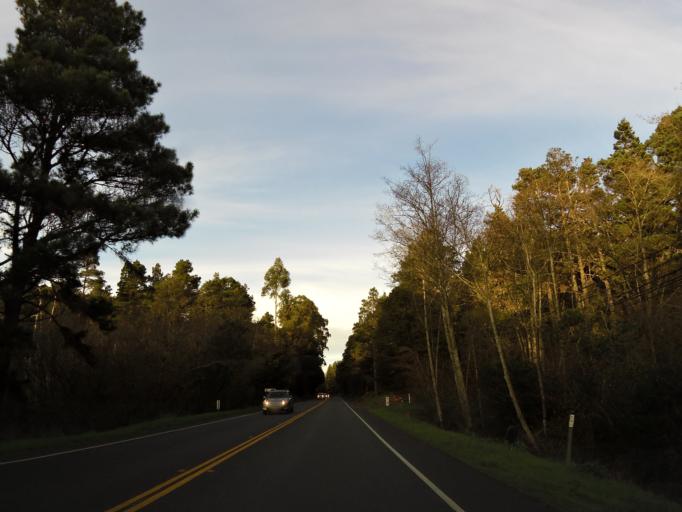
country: US
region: California
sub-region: Mendocino County
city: Fort Bragg
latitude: 39.3931
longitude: -123.8106
